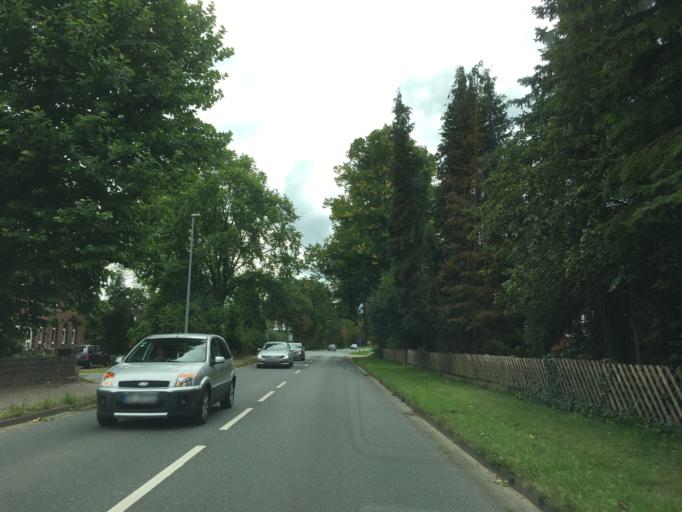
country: DE
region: Lower Saxony
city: Embsen
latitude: 53.2120
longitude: 10.3679
